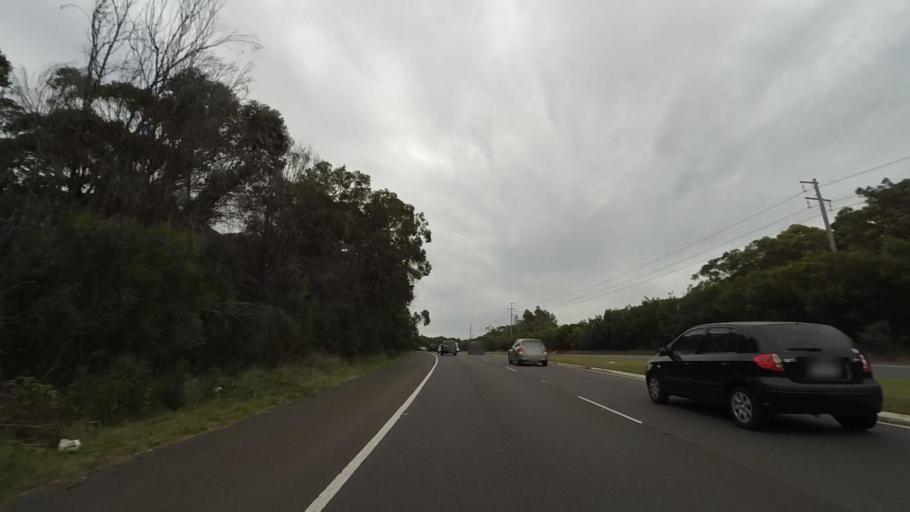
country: AU
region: New South Wales
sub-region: Sutherland Shire
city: Loftus
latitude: -34.0418
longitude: 151.0569
